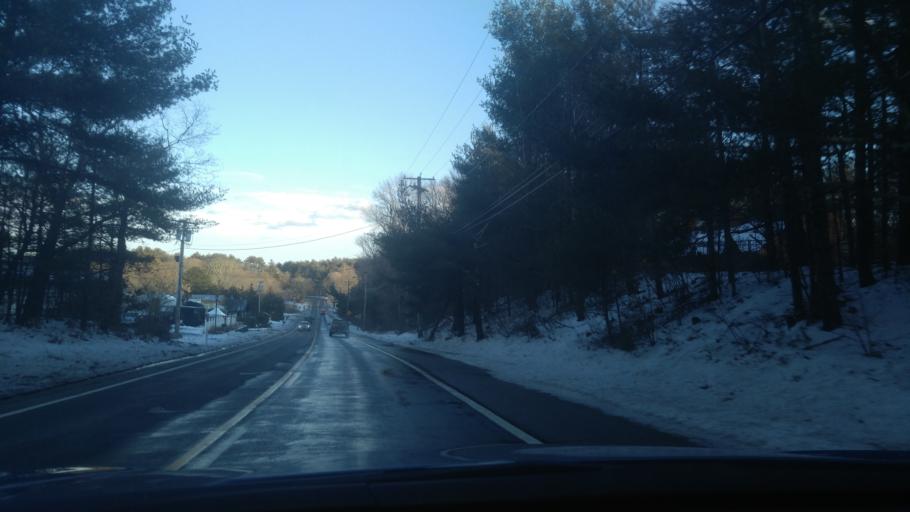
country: US
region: Rhode Island
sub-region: Kent County
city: Coventry
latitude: 41.7033
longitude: -71.6391
